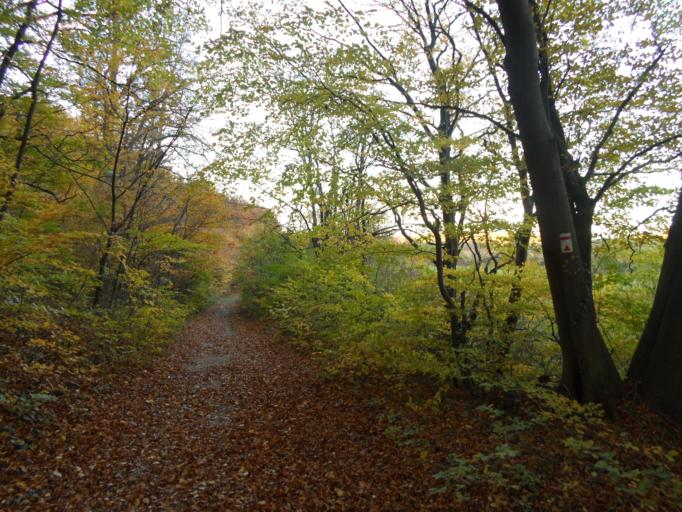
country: HU
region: Veszprem
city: Herend
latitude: 47.1100
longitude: 17.7973
